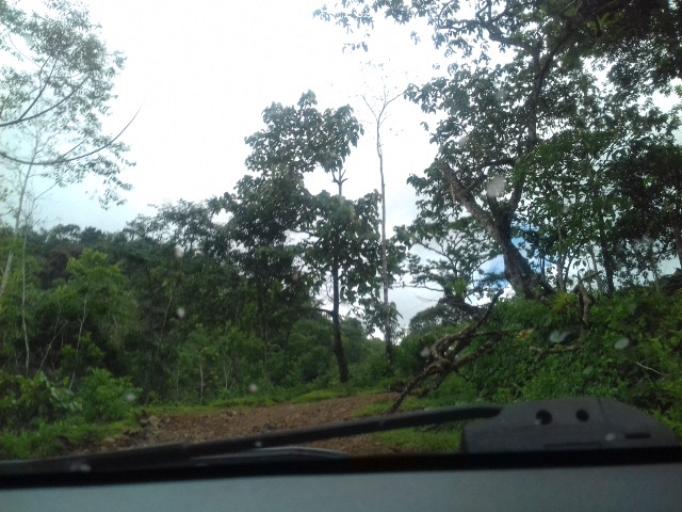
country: NI
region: Matagalpa
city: Rio Blanco
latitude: 13.0331
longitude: -85.2344
